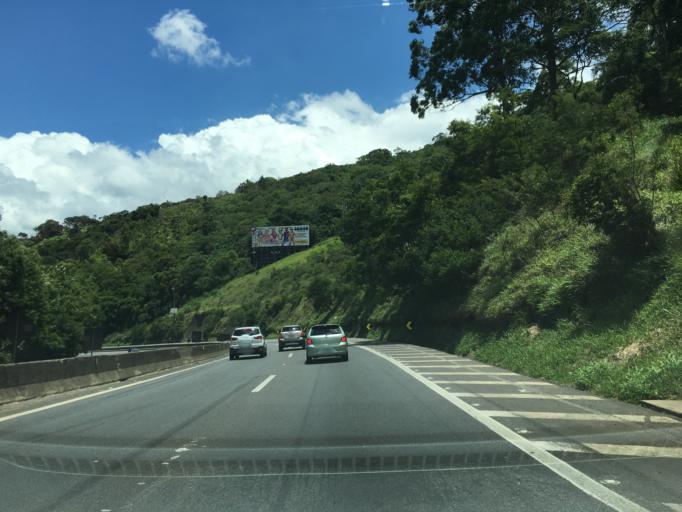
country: BR
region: Sao Paulo
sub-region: Mairipora
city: Mairipora
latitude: -23.2906
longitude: -46.5801
